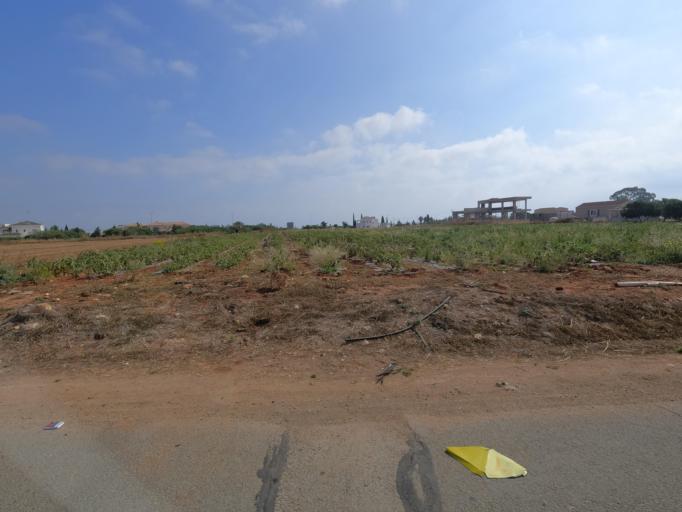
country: CY
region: Ammochostos
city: Paralimni
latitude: 35.0285
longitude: 34.0051
